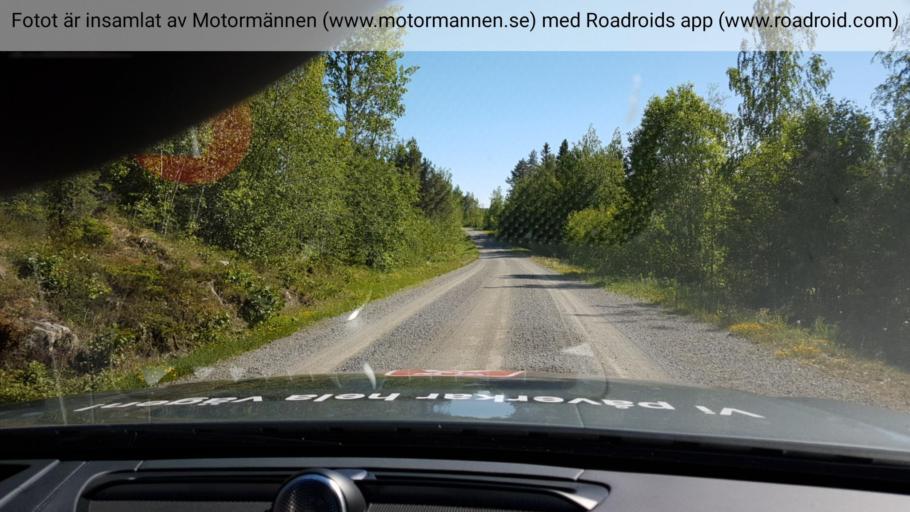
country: SE
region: Jaemtland
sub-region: Bergs Kommun
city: Hoverberg
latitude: 62.7559
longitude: 14.6627
